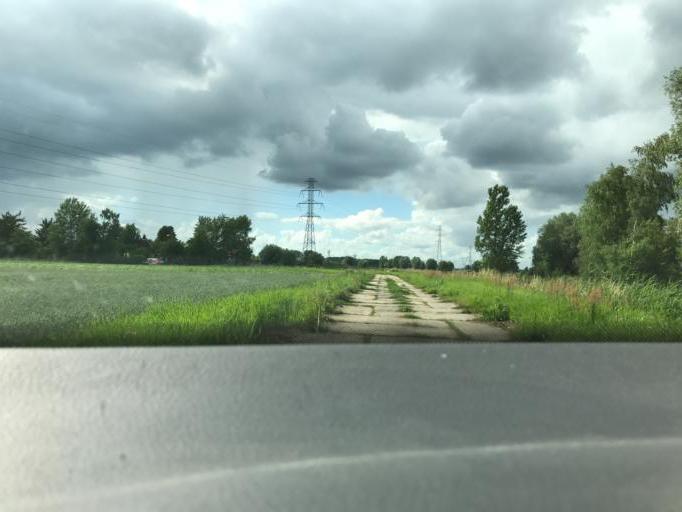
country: PL
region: Pomeranian Voivodeship
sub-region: Gdansk
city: Gdansk
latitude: 54.3065
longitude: 18.7289
